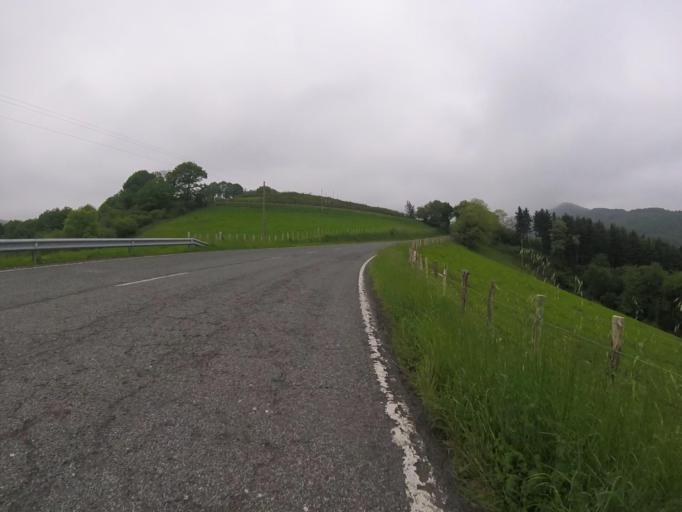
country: ES
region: Navarre
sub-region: Provincia de Navarra
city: Zugarramurdi
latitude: 43.2647
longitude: -1.4929
